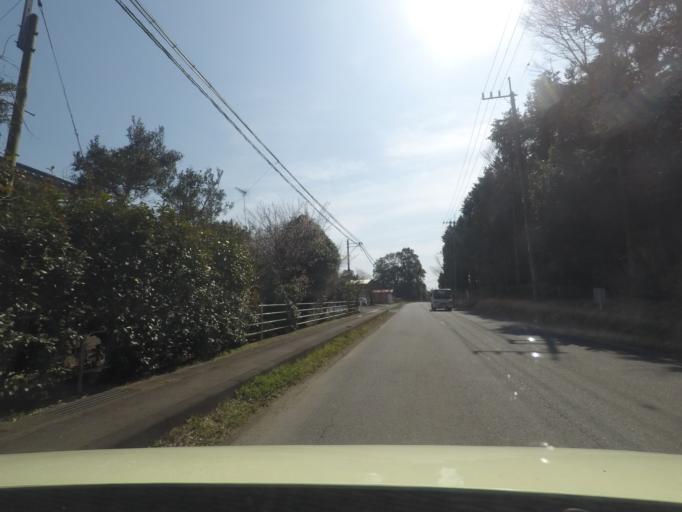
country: JP
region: Ibaraki
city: Ishioka
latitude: 36.2025
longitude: 140.3210
